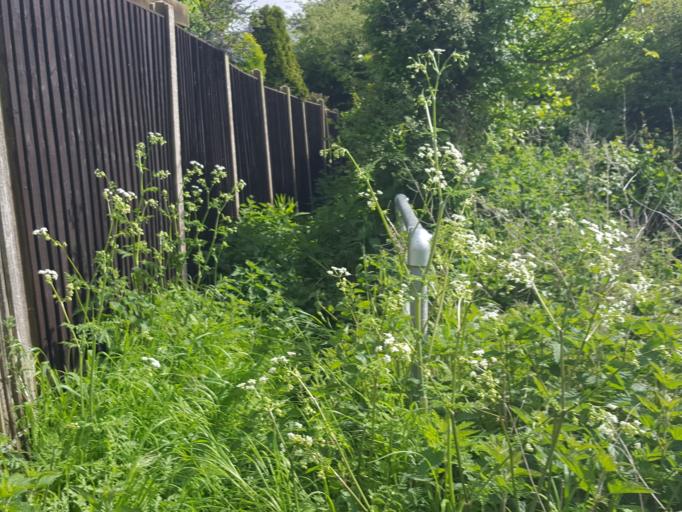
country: GB
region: England
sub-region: Essex
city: Frinton-on-Sea
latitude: 51.8351
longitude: 1.2082
